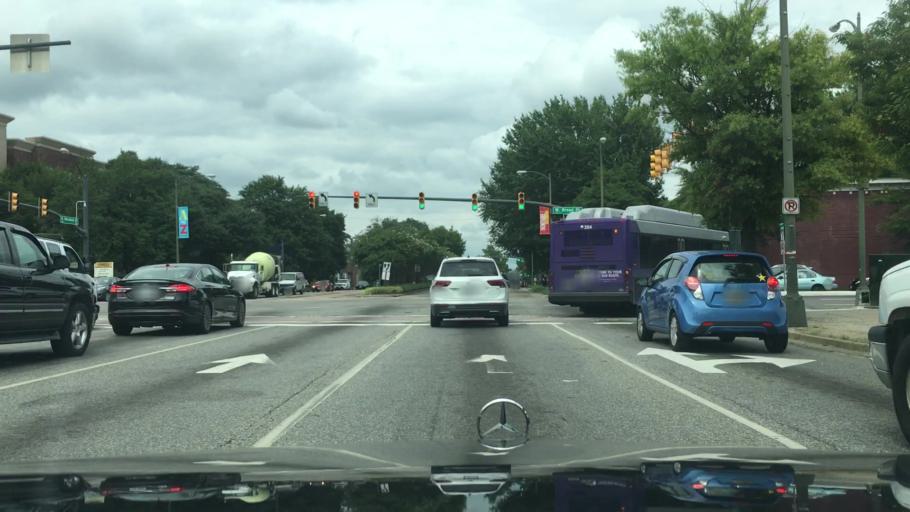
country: US
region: Virginia
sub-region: City of Richmond
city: Richmond
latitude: 37.5485
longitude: -77.4475
